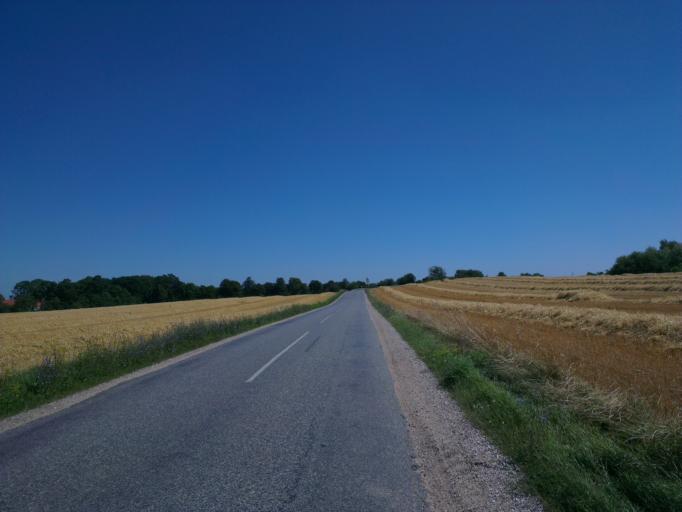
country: DK
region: Capital Region
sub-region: Egedal Kommune
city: Olstykke
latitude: 55.8335
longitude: 12.1329
